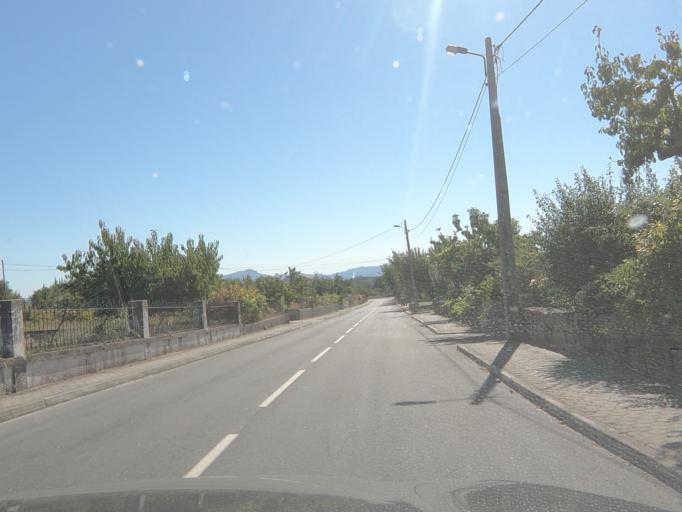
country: PT
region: Vila Real
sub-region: Valpacos
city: Valpacos
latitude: 41.6589
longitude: -7.3202
